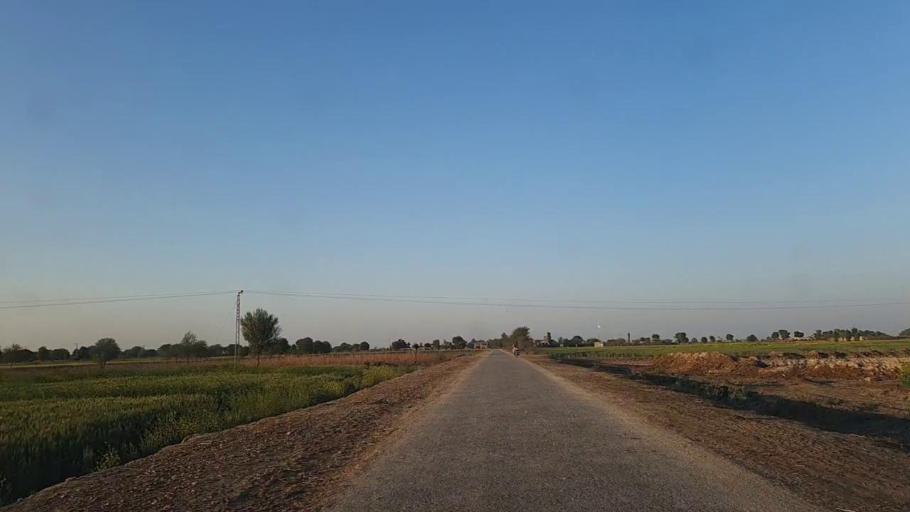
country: PK
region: Sindh
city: Naukot
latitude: 25.0292
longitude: 69.4168
